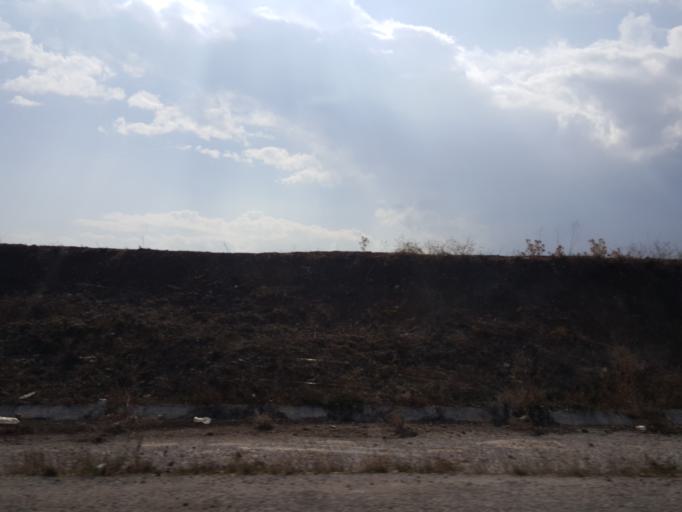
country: TR
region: Corum
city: Alaca
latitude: 40.1384
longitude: 34.7960
